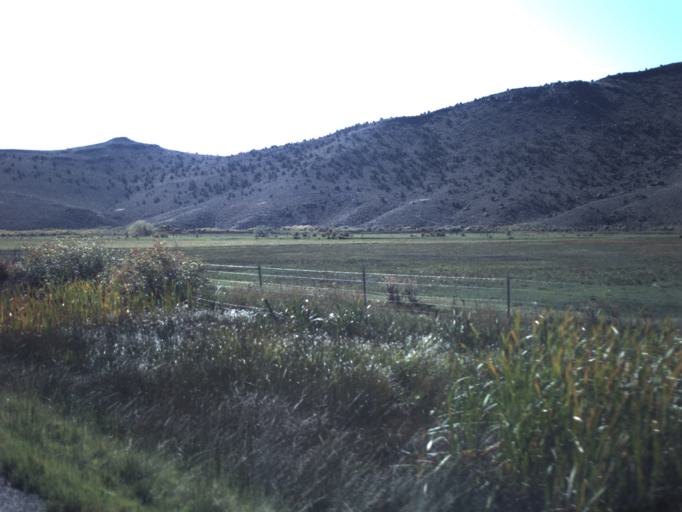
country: US
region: Utah
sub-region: Piute County
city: Junction
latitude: 38.1674
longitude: -112.0392
